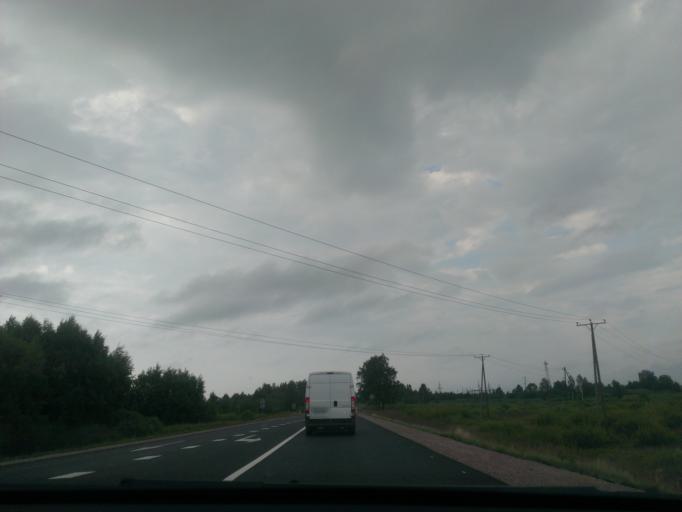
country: LV
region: Lecava
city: Iecava
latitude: 56.6242
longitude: 24.2202
